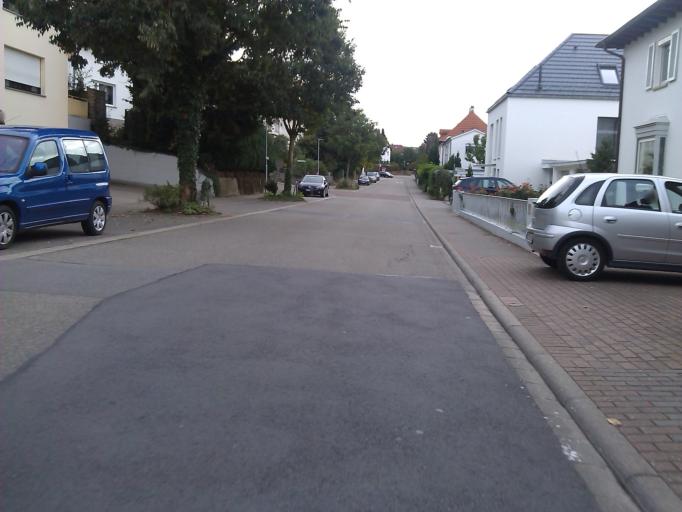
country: DE
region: Baden-Wuerttemberg
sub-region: Karlsruhe Region
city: Weinheim
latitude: 49.5344
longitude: 8.6649
